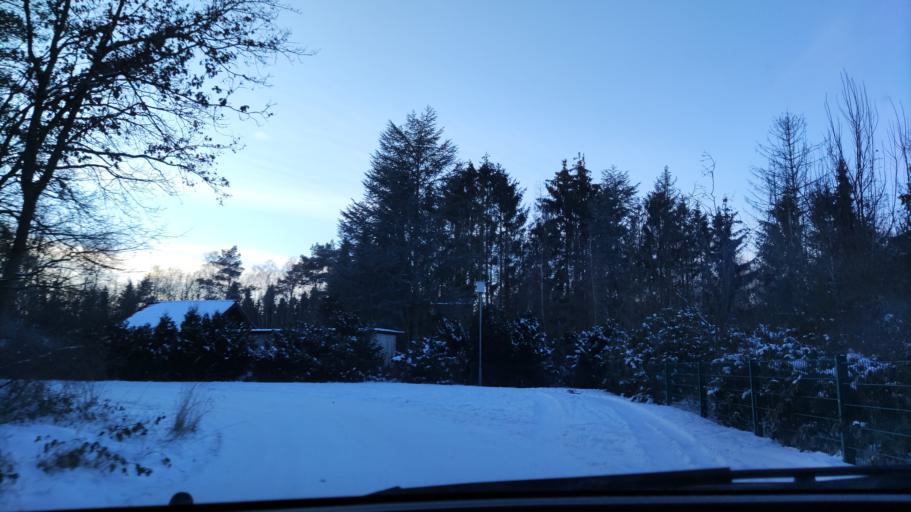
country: DE
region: Lower Saxony
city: Bleckede
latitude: 53.2963
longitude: 10.6851
